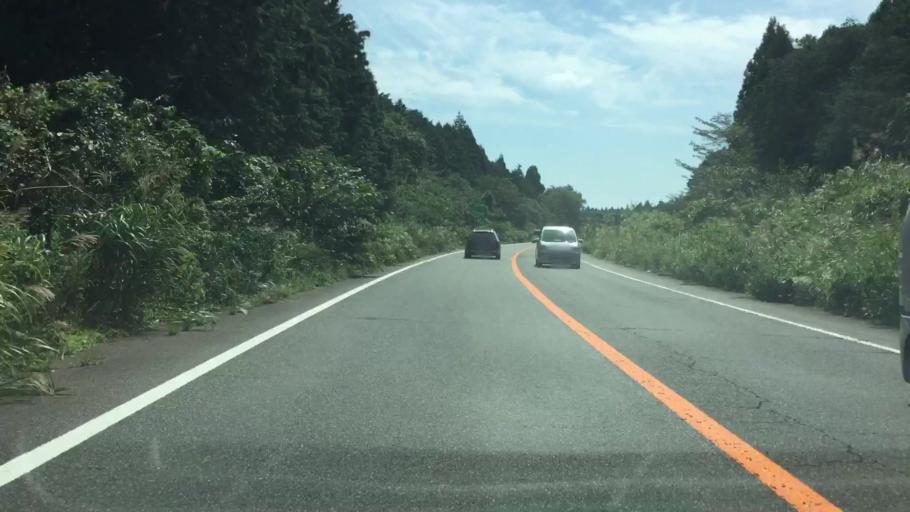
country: JP
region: Shizuoka
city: Fujinomiya
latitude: 35.3241
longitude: 138.5902
